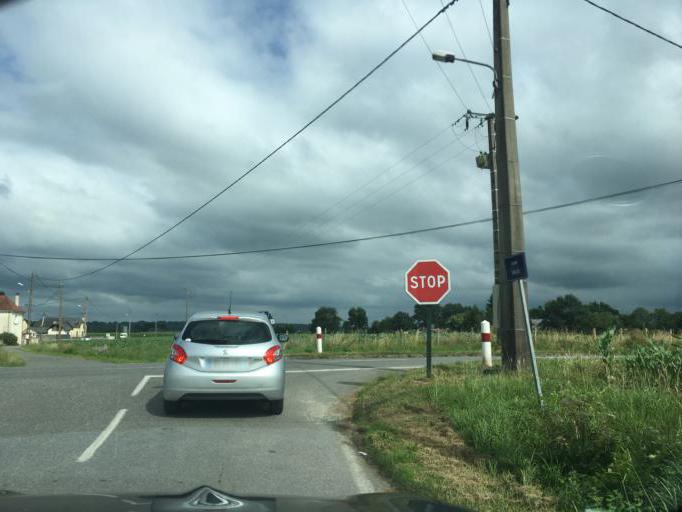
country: FR
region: Aquitaine
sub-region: Departement des Pyrenees-Atlantiques
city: Ousse
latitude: 43.3115
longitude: -0.2755
